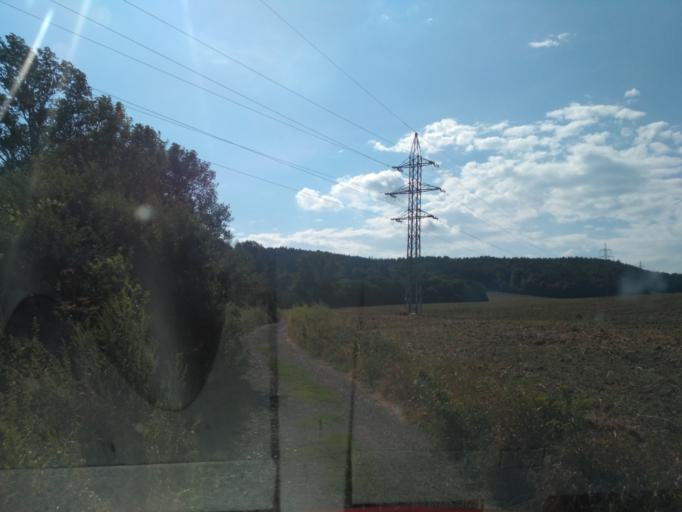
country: SK
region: Kosicky
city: Kosice
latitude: 48.8476
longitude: 21.2583
